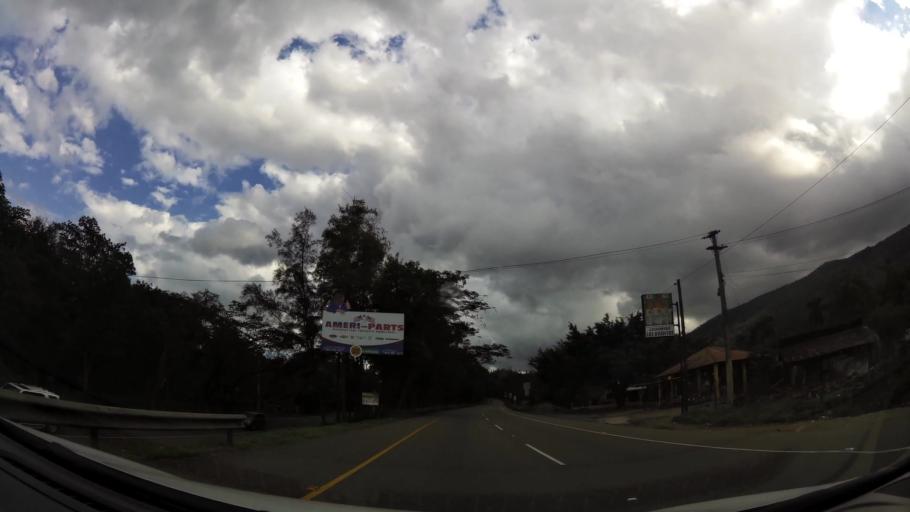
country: DO
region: La Vega
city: Rincon
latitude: 19.1288
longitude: -70.4552
